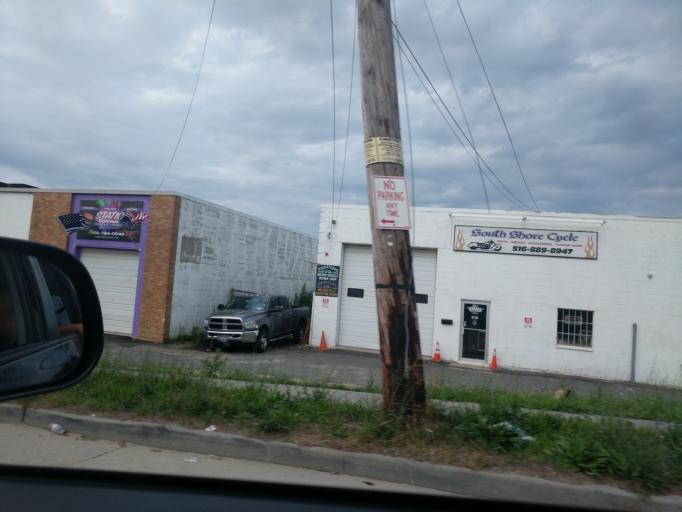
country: US
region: New York
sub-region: Nassau County
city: Island Park
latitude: 40.6223
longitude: -73.6505
